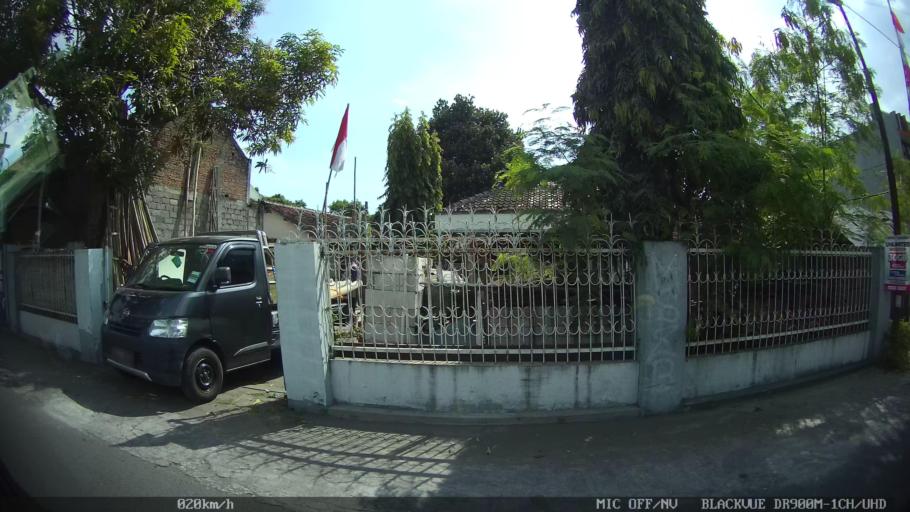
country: ID
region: Daerah Istimewa Yogyakarta
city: Kasihan
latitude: -7.8136
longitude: 110.3282
